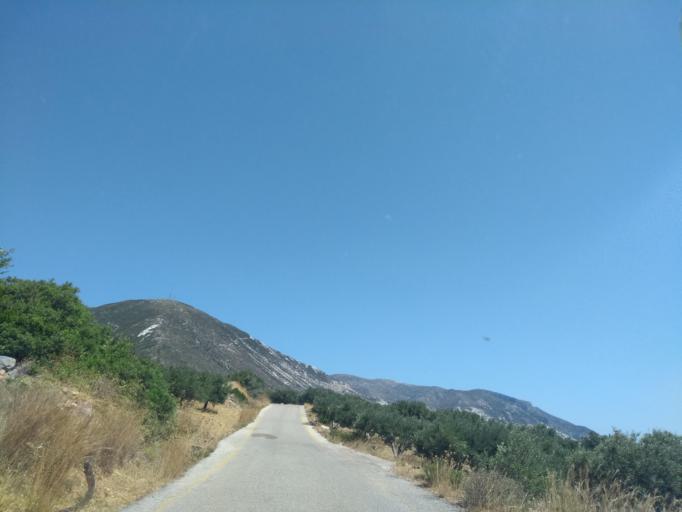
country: GR
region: Crete
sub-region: Nomos Chanias
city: Vryses
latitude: 35.3586
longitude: 23.5426
